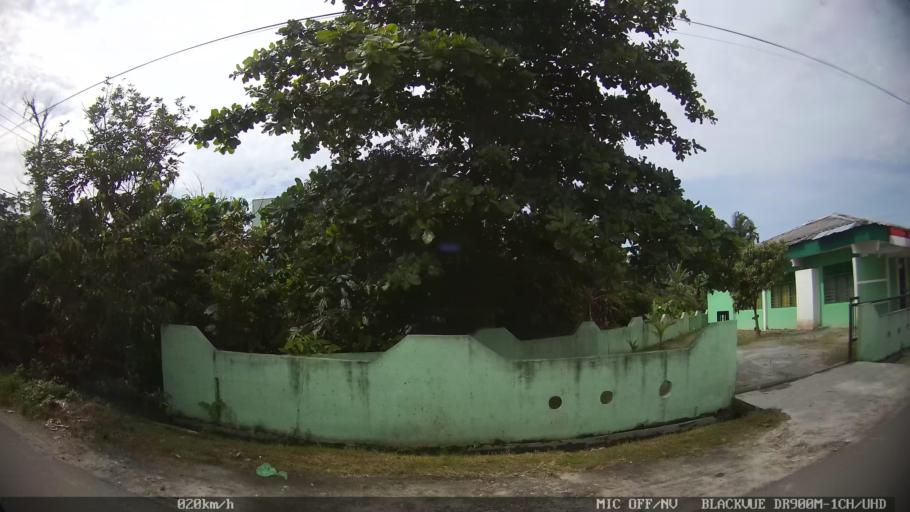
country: ID
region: North Sumatra
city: Percut
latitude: 3.6199
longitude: 98.7987
